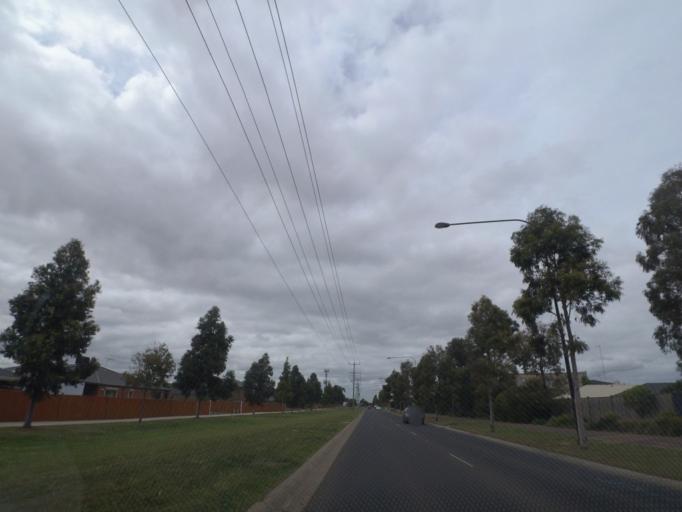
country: AU
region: Victoria
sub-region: Melton
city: Burnside Heights
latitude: -37.7233
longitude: 144.7451
